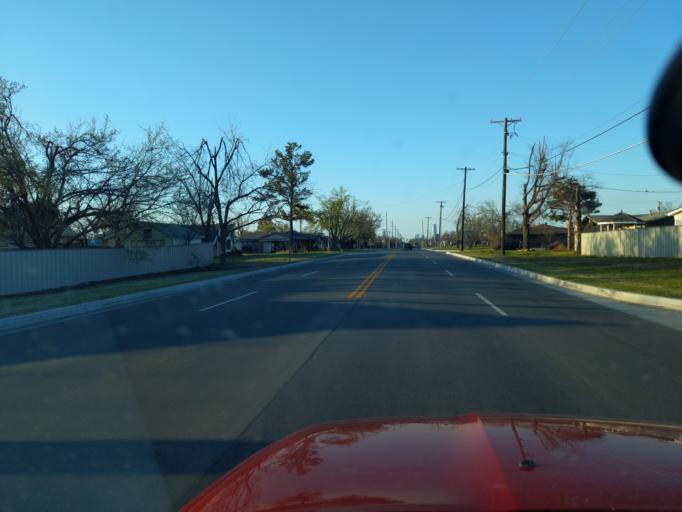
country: US
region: Oklahoma
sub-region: Oklahoma County
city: Oklahoma City
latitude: 35.4030
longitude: -97.5213
